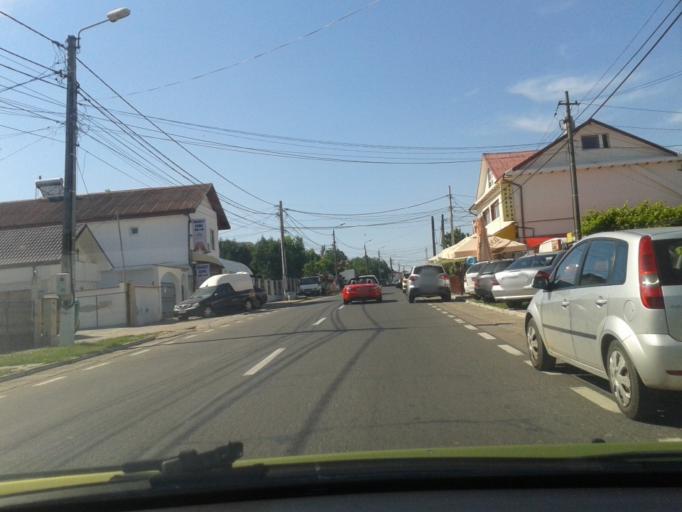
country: RO
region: Constanta
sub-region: Municipiul Mangalia
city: Mangalia
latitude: 43.7852
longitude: 28.5780
